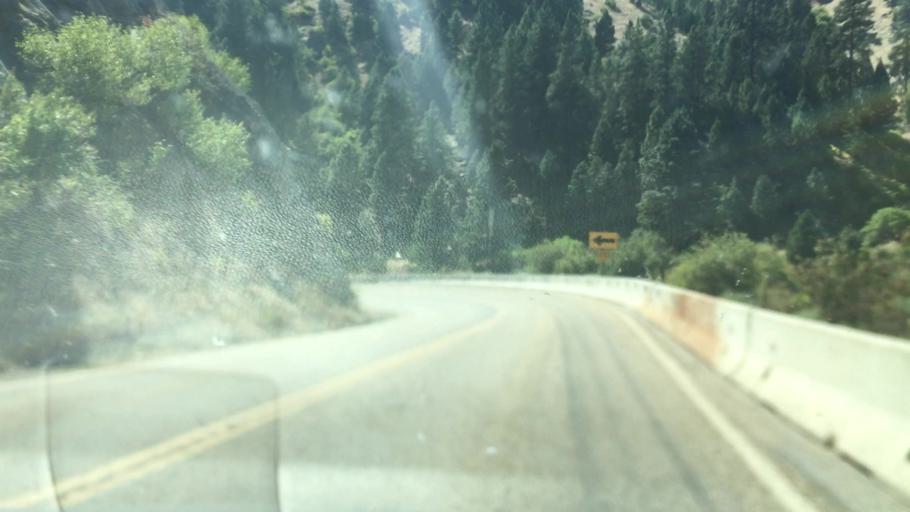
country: US
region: Idaho
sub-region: Boise County
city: Idaho City
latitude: 44.0992
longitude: -116.0985
